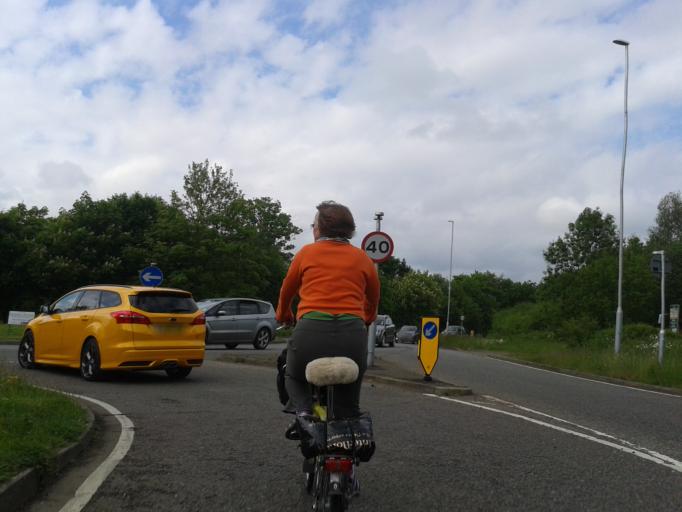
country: GB
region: England
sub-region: Northamptonshire
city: Oundle
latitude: 52.4879
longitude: -0.4589
